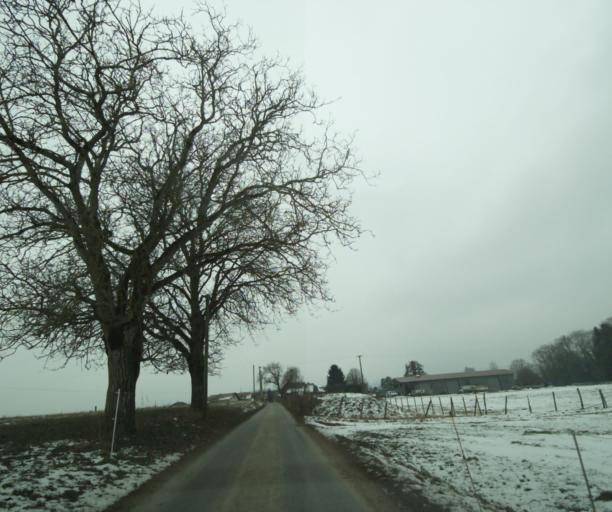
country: FR
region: Rhone-Alpes
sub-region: Departement de la Haute-Savoie
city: Reignier-Esery
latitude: 46.1406
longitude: 6.2898
